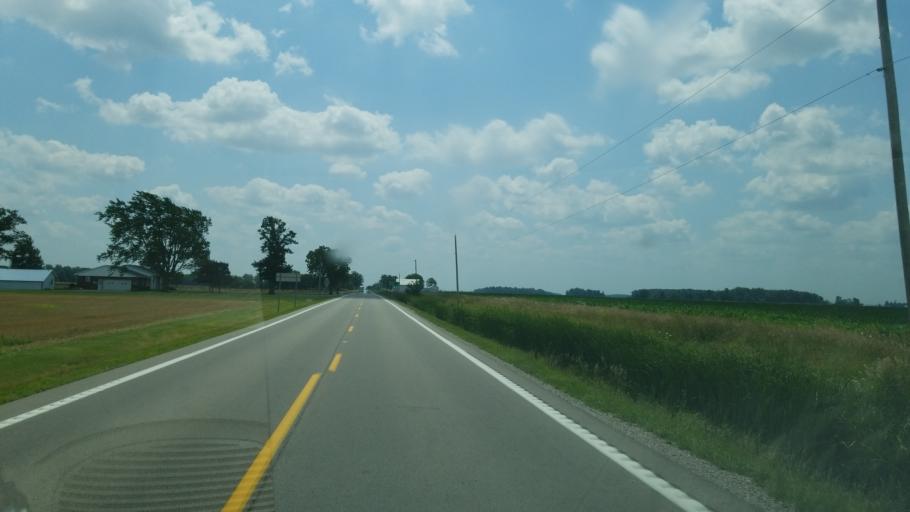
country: US
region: Ohio
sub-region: Henry County
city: Deshler
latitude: 41.2828
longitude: -83.9408
